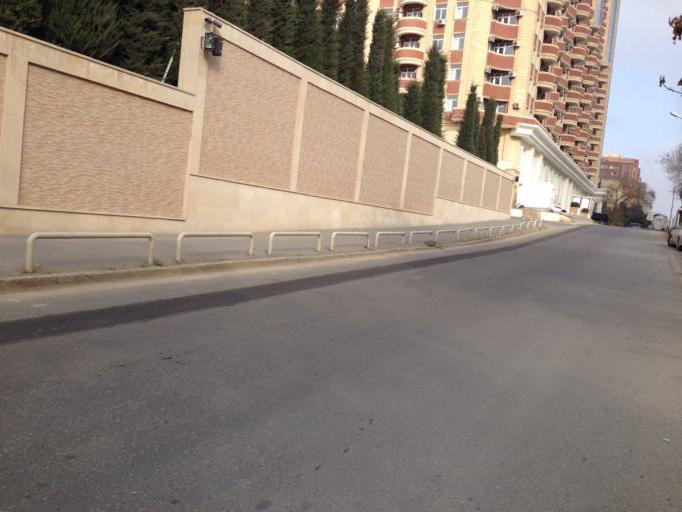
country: AZ
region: Baki
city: Baku
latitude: 40.3960
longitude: 49.8584
